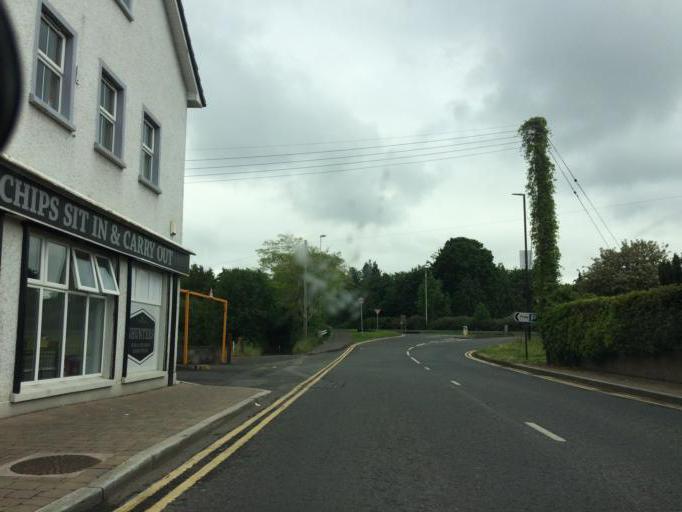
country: GB
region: Northern Ireland
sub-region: Antrim Borough
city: Antrim
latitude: 54.7129
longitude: -6.2198
